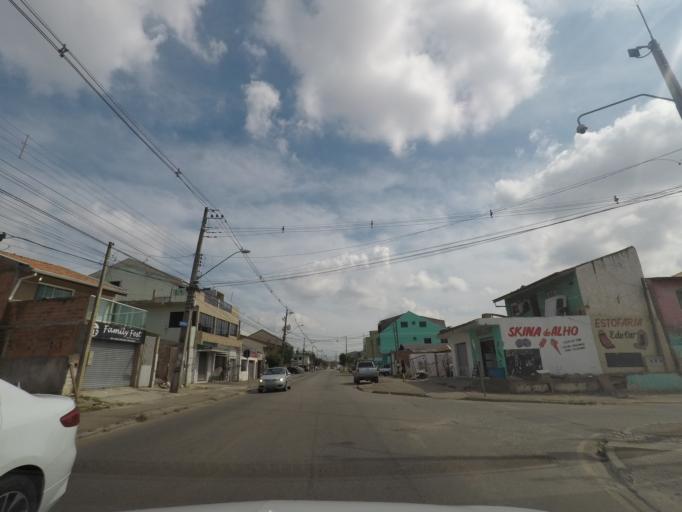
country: BR
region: Parana
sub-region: Pinhais
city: Pinhais
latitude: -25.4654
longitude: -49.1918
